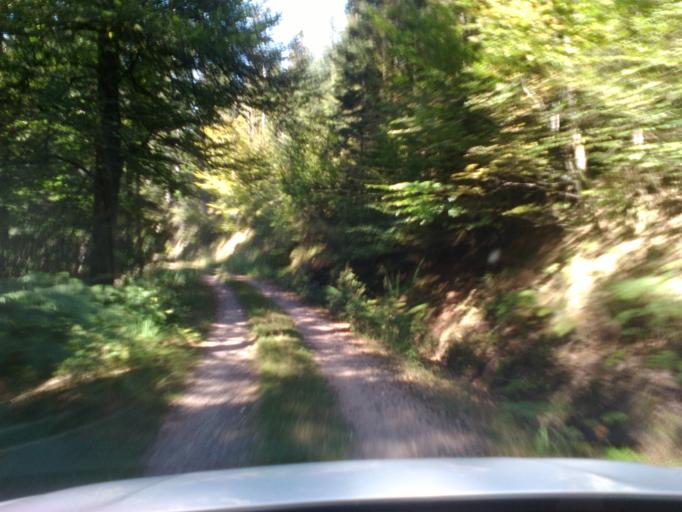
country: FR
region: Lorraine
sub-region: Departement des Vosges
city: Senones
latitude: 48.4358
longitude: 6.9918
